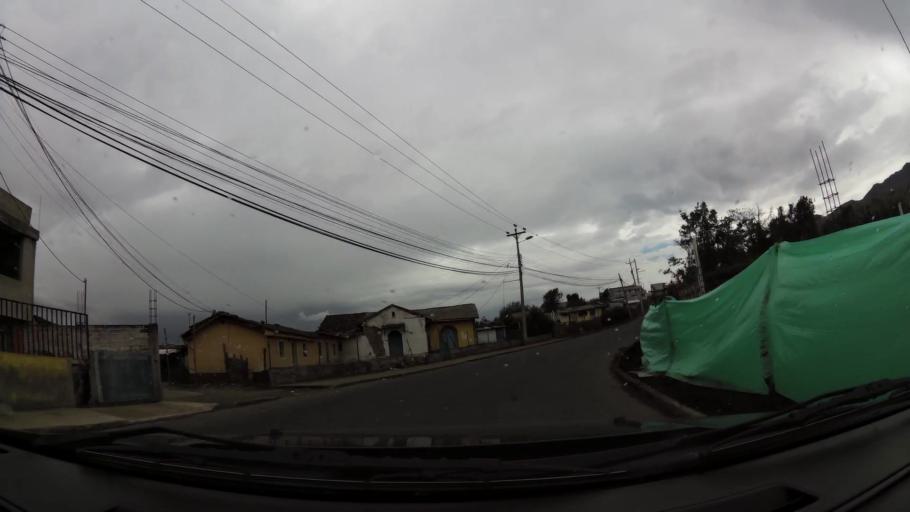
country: EC
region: Pichincha
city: Sangolqui
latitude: -0.3451
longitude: -78.5537
